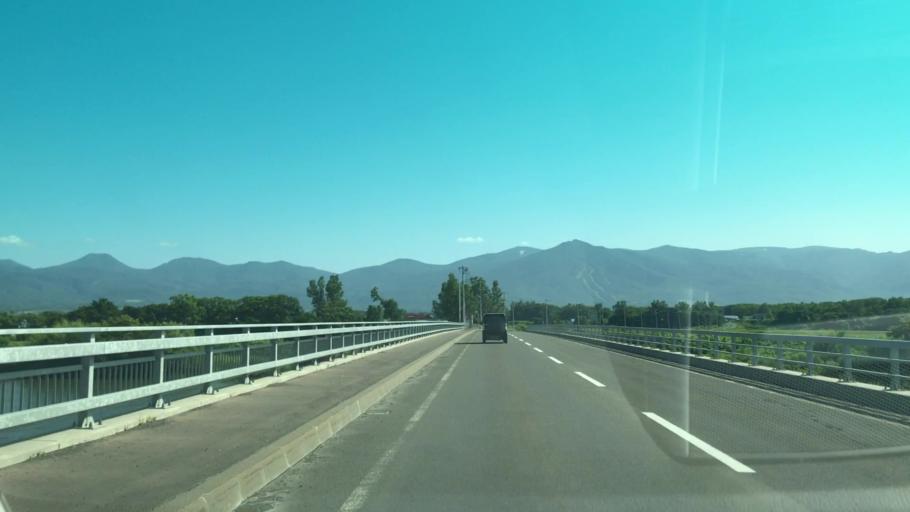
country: JP
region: Hokkaido
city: Iwanai
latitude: 43.0225
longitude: 140.5482
